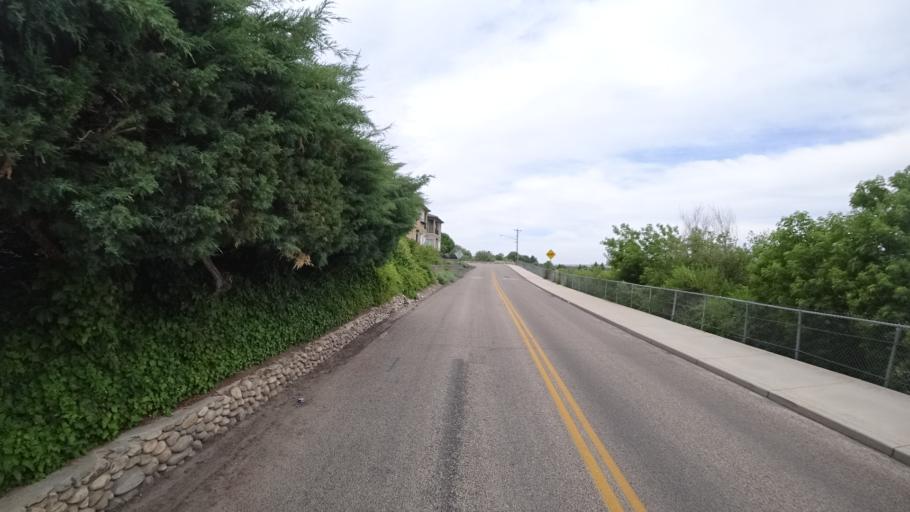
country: US
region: Idaho
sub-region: Ada County
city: Boise
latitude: 43.6034
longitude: -116.2158
